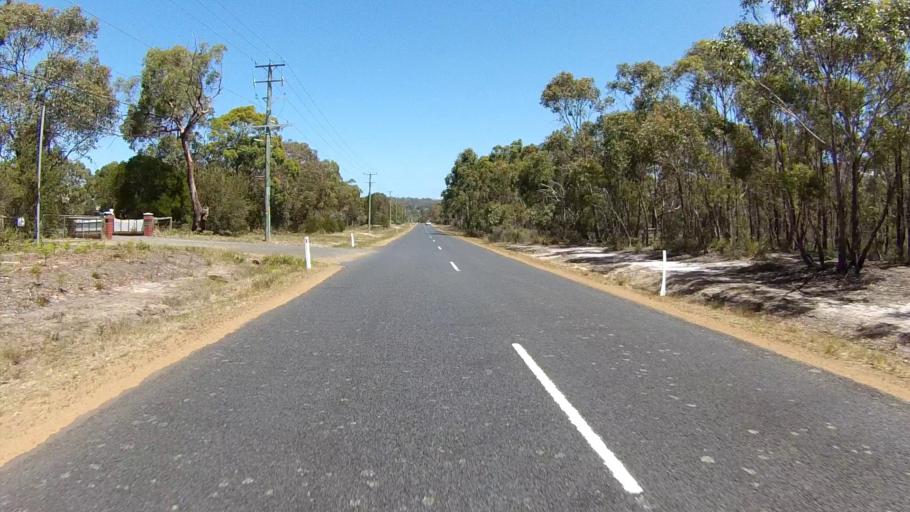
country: AU
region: Tasmania
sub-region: Clarence
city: Sandford
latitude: -42.9831
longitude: 147.4838
